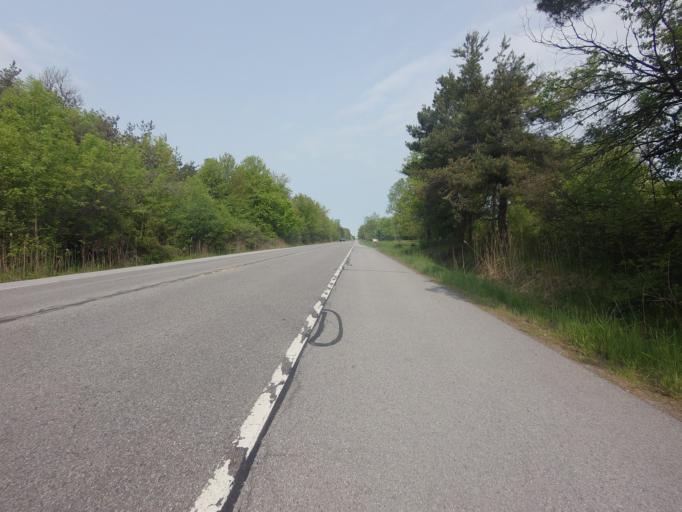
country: US
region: New York
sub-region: Jefferson County
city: Dexter
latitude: 44.0161
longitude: -76.0249
